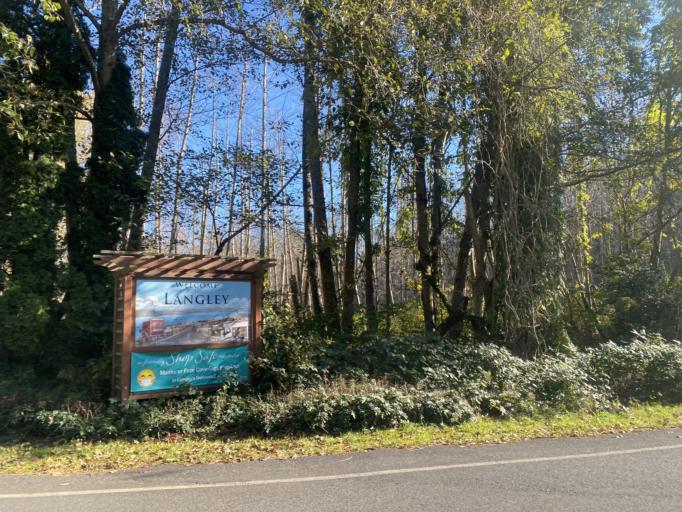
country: US
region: Washington
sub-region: Island County
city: Langley
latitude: 48.0375
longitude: -122.4200
